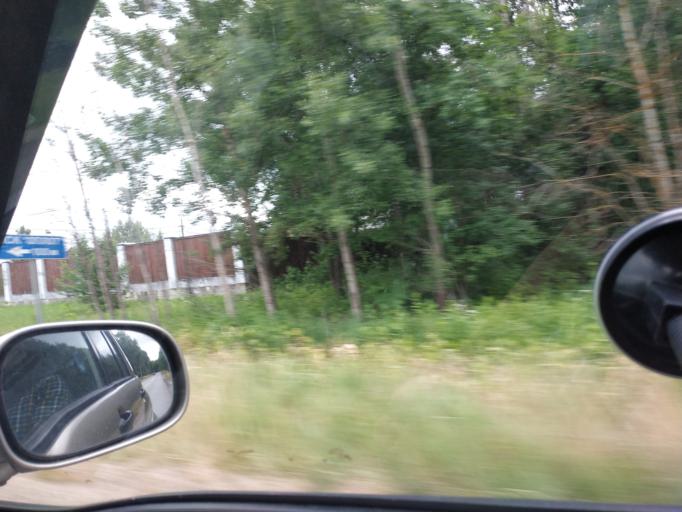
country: RU
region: Moskovskaya
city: Krasnoarmeysk
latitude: 56.0784
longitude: 38.2428
